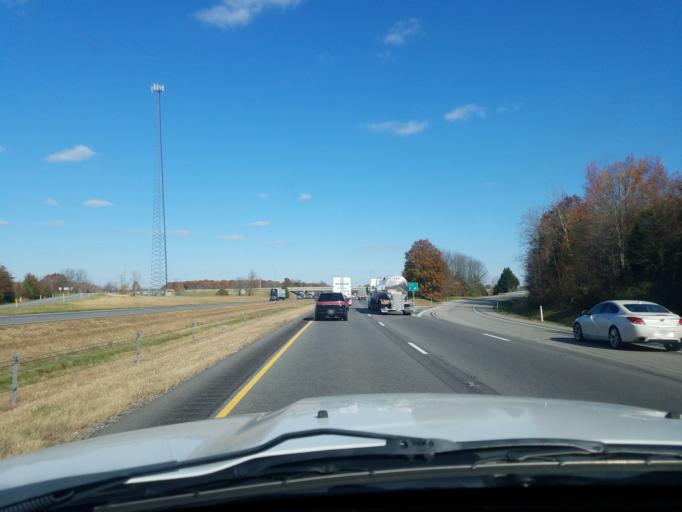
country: US
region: Indiana
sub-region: Jackson County
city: Crothersville
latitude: 38.8405
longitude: -85.8165
